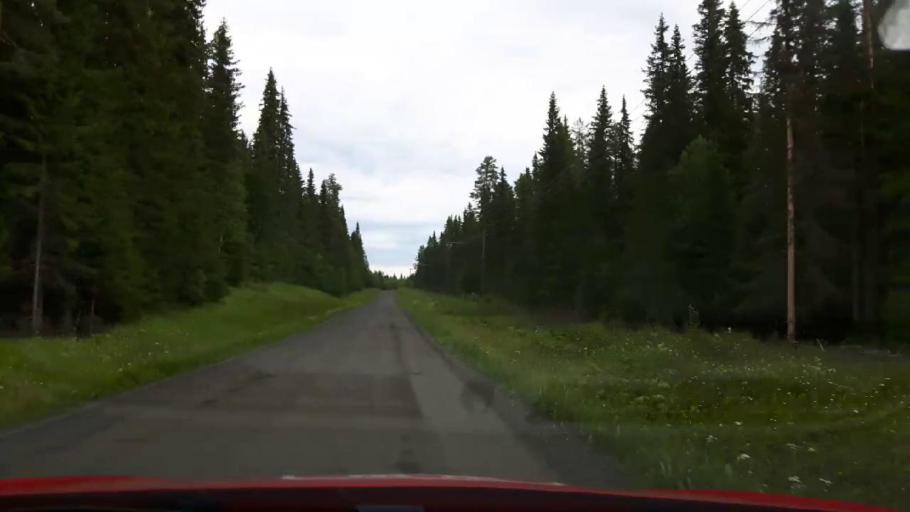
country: SE
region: Jaemtland
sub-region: Stroemsunds Kommun
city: Stroemsund
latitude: 63.4656
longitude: 15.2853
